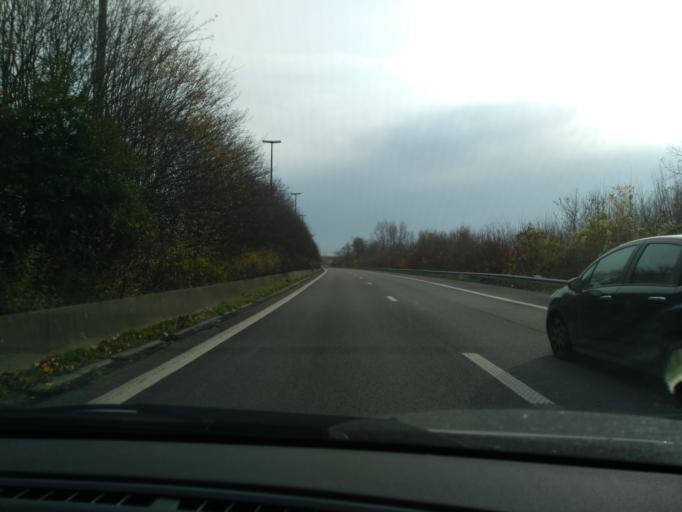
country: BE
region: Wallonia
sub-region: Province du Hainaut
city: Antoing
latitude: 50.5623
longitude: 3.4935
